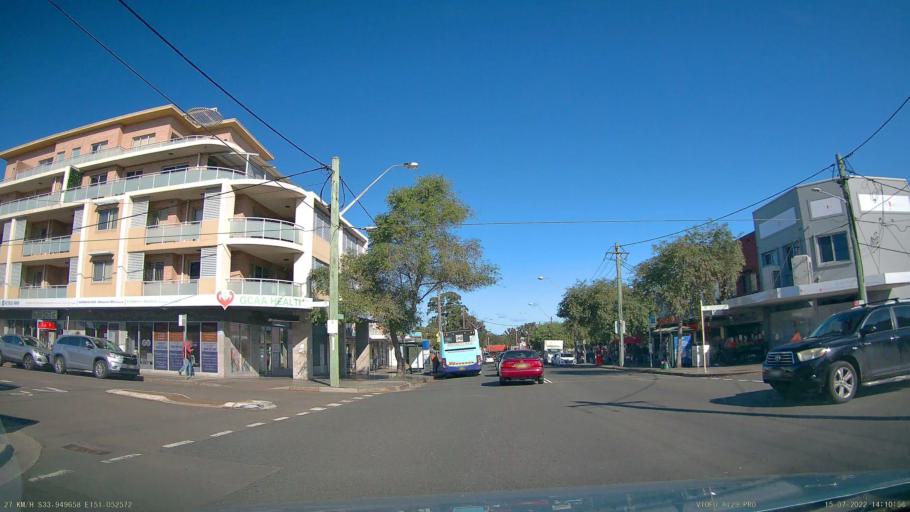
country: AU
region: New South Wales
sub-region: Hurstville
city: Peakhurst
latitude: -33.9498
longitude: 151.0525
